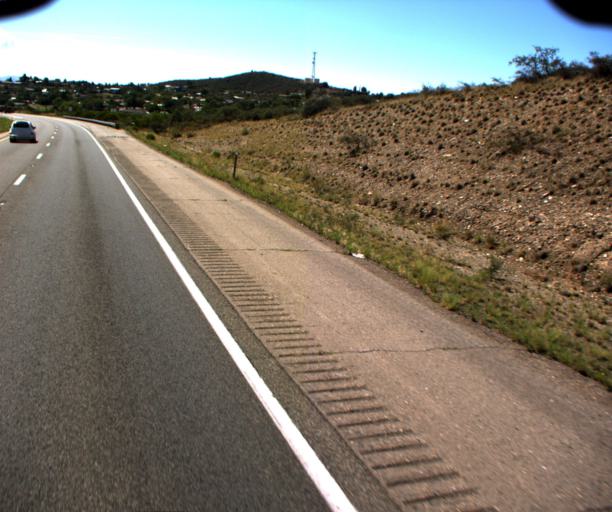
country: US
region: Arizona
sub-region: Yavapai County
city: Mayer
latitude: 34.4033
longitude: -112.2375
